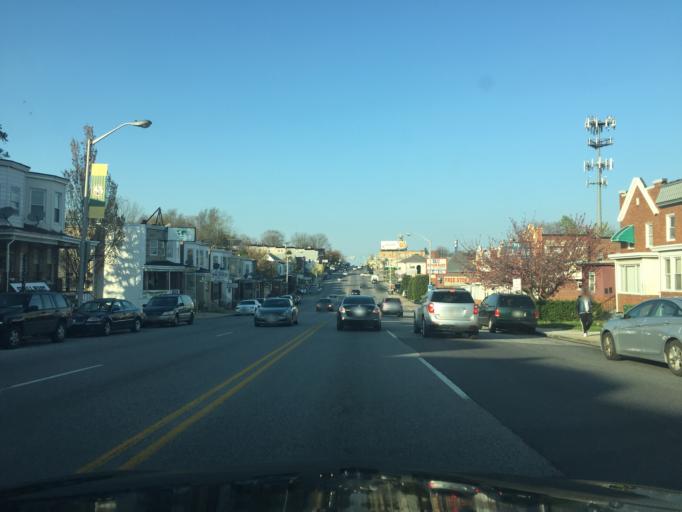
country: US
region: Maryland
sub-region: Baltimore County
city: Rosedale
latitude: 39.3358
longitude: -76.5549
